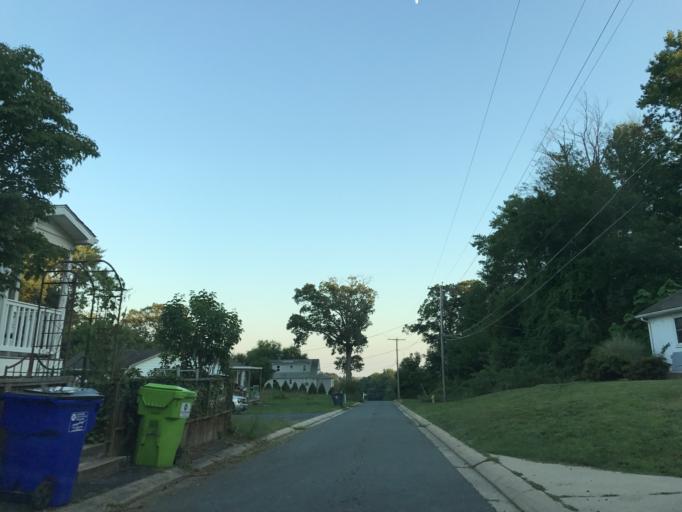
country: US
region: Maryland
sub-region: Harford County
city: Joppatowne
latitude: 39.4317
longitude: -76.3707
